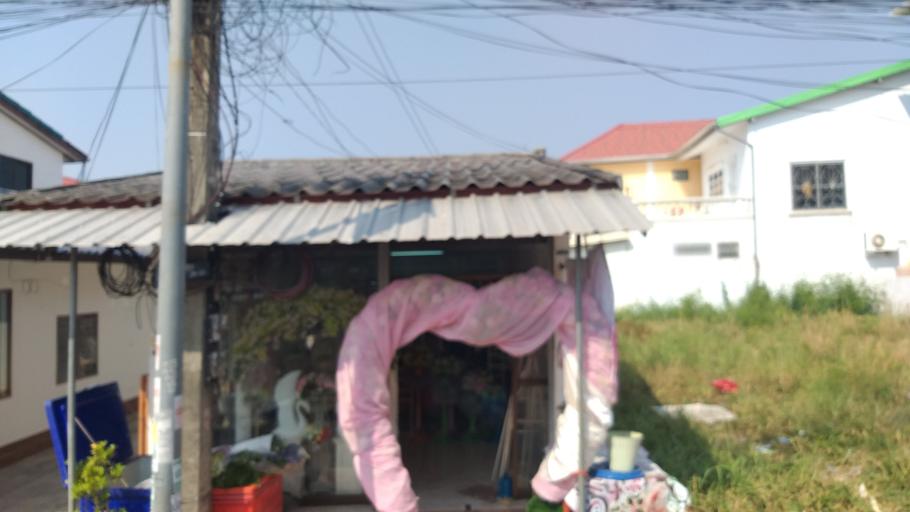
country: TH
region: Changwat Udon Thani
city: Nong Han
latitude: 17.3629
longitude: 103.1020
